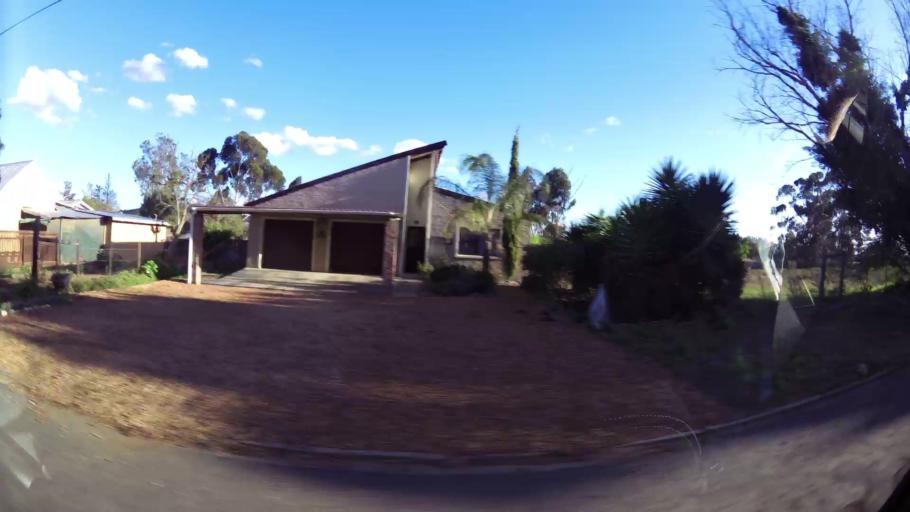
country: ZA
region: Western Cape
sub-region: Eden District Municipality
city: Riversdale
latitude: -34.0861
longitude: 20.9493
